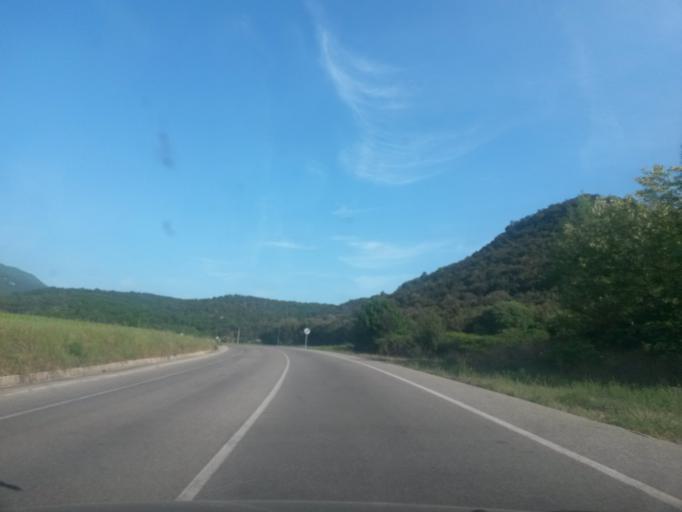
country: ES
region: Catalonia
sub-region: Provincia de Girona
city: les Planes d'Hostoles
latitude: 42.0429
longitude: 2.5642
